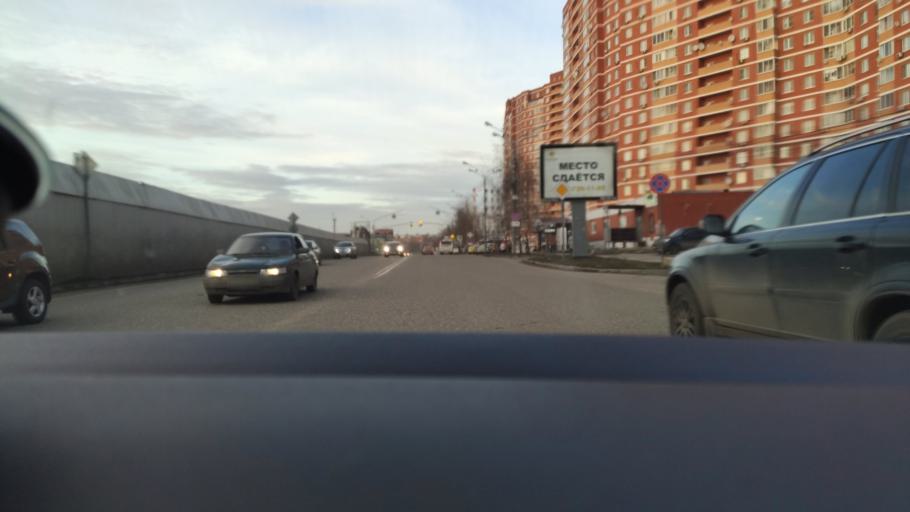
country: RU
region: Moskovskaya
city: Vidnoye
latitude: 55.5420
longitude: 37.7200
